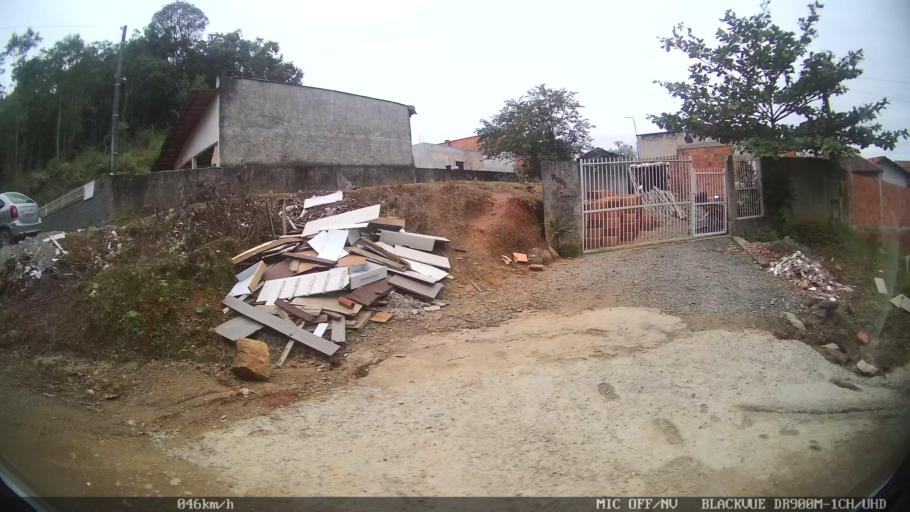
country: BR
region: Santa Catarina
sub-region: Joinville
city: Joinville
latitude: -26.2729
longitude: -48.9035
